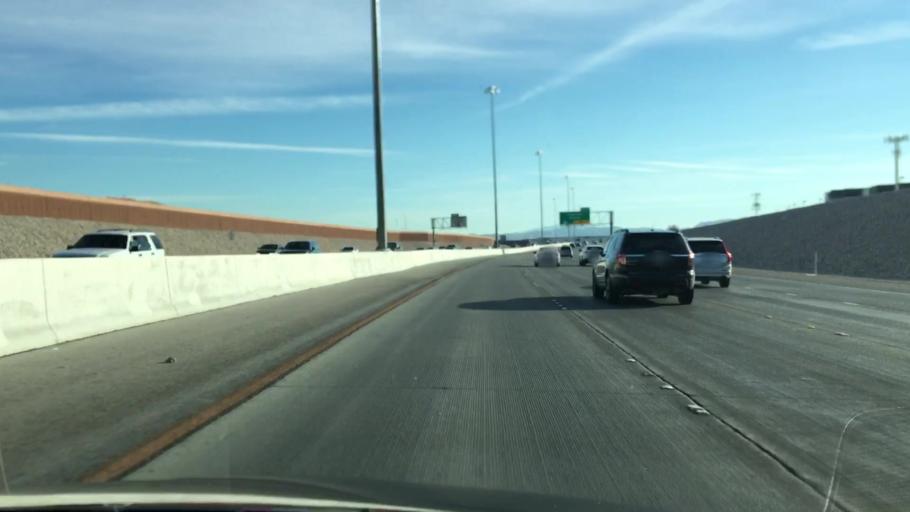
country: US
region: Nevada
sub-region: Clark County
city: Summerlin South
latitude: 36.1070
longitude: -115.2960
